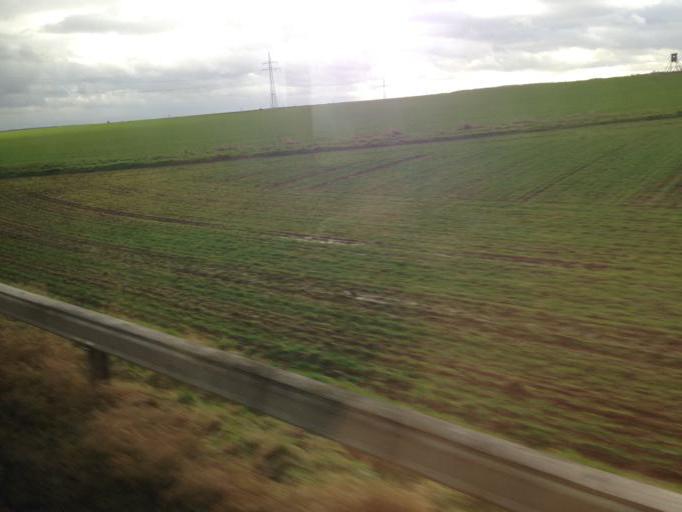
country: DE
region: Hesse
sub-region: Regierungsbezirk Giessen
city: Lich
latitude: 50.5072
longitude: 8.8438
